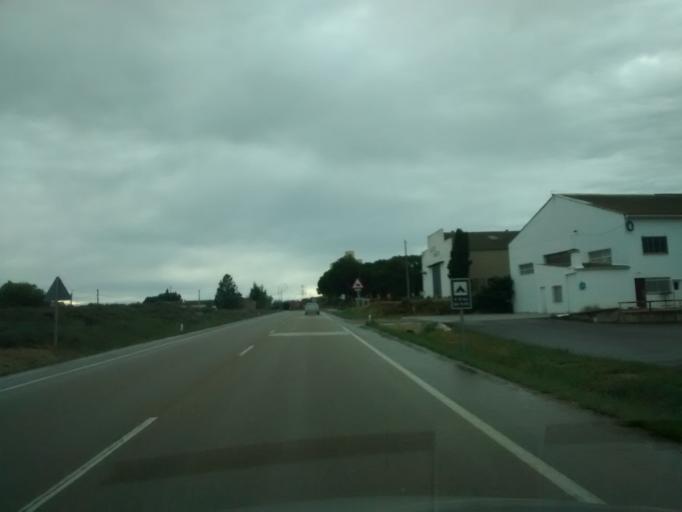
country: ES
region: Aragon
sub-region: Provincia de Zaragoza
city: Caspe
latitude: 41.2246
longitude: -0.0262
